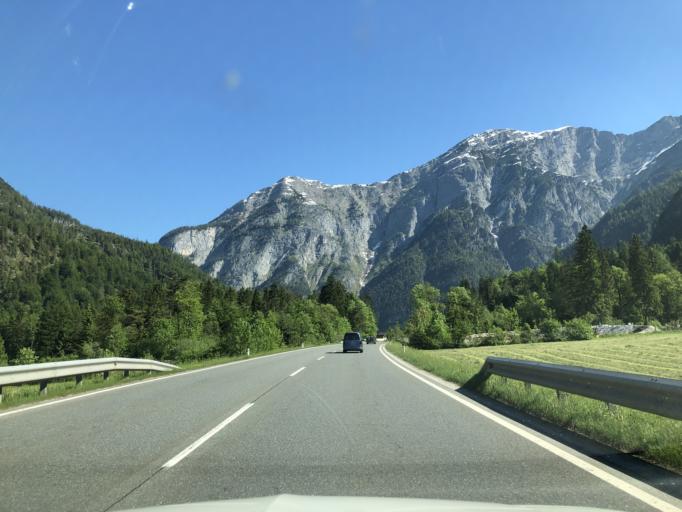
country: AT
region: Salzburg
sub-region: Politischer Bezirk Zell am See
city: Saalfelden am Steinernen Meer
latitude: 47.4660
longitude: 12.8279
